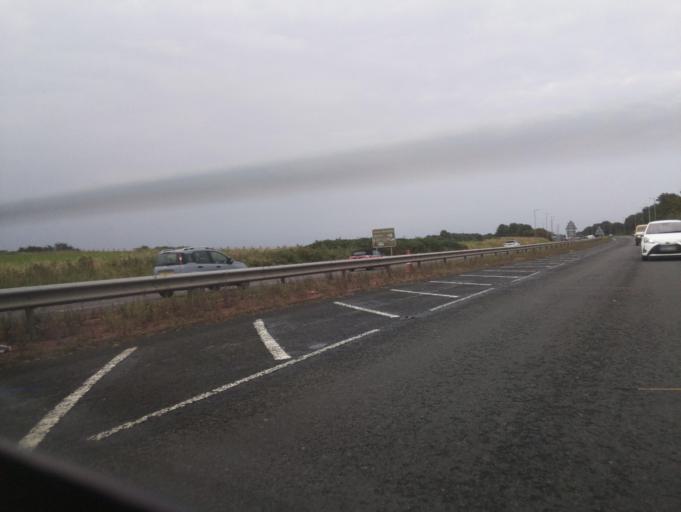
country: GB
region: Scotland
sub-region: Dumfries and Galloway
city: Gretna
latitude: 54.9961
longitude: -3.0877
